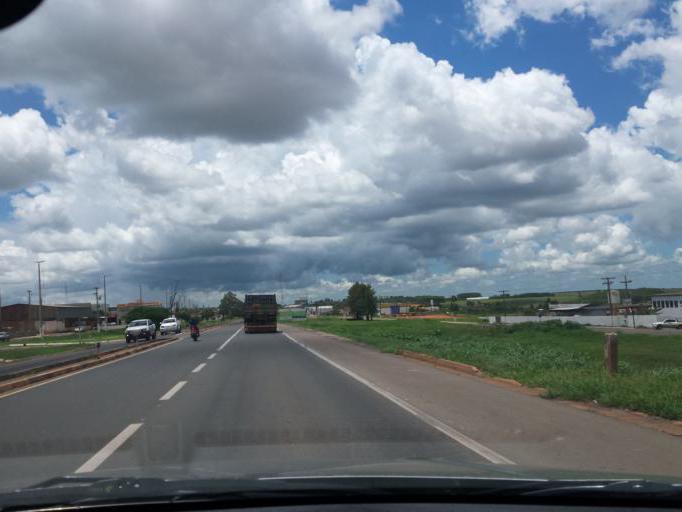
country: BR
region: Goias
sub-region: Cristalina
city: Cristalina
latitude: -16.7626
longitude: -47.6132
